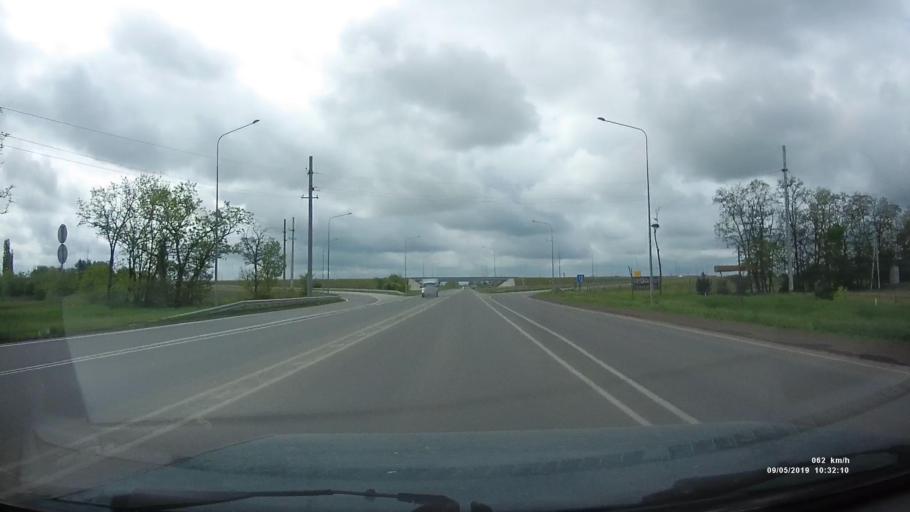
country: RU
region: Rostov
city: Azov
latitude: 47.0750
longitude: 39.4267
